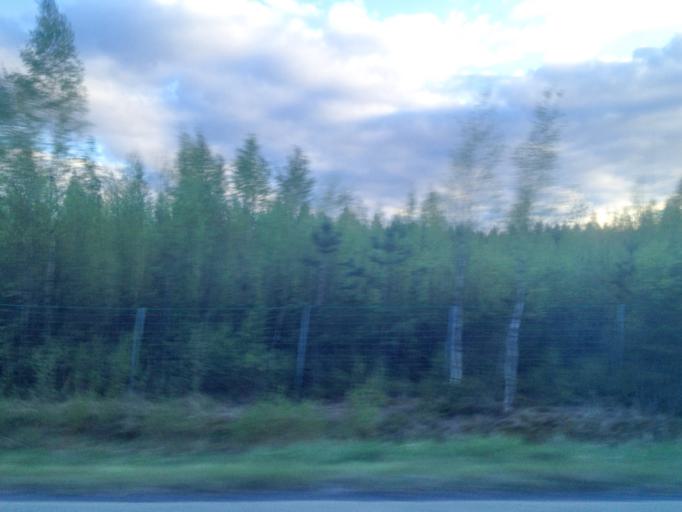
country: FI
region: Haeme
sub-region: Haemeenlinna
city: Kalvola
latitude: 61.1131
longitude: 24.1361
